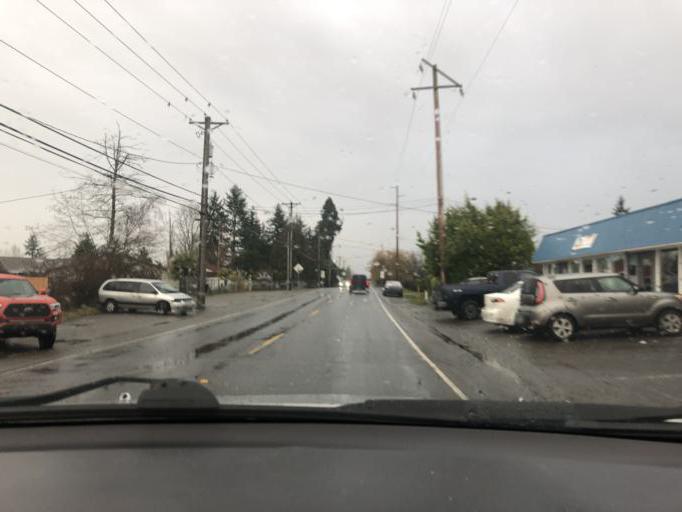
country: US
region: Washington
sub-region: Pierce County
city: Waller
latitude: 47.1989
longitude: -122.3891
